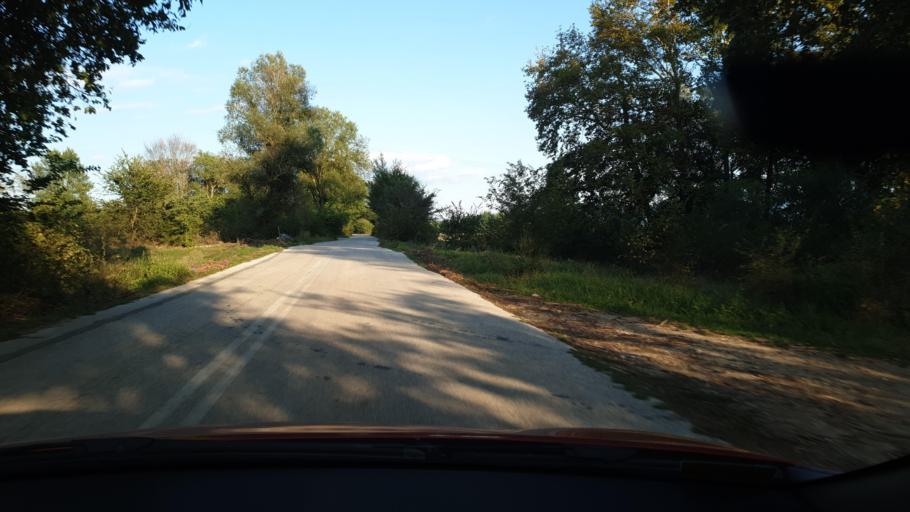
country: GR
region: Central Macedonia
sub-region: Nomos Chalkidikis
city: Galatista
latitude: 40.5632
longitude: 23.3382
